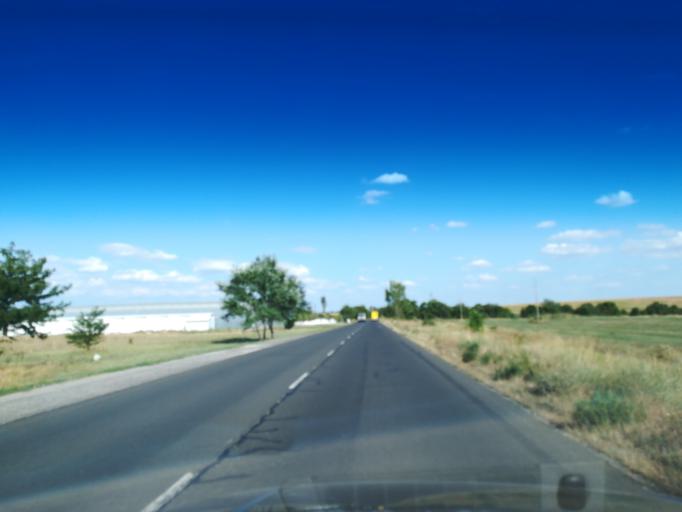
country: BG
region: Stara Zagora
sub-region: Obshtina Chirpan
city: Chirpan
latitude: 42.0713
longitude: 25.2058
